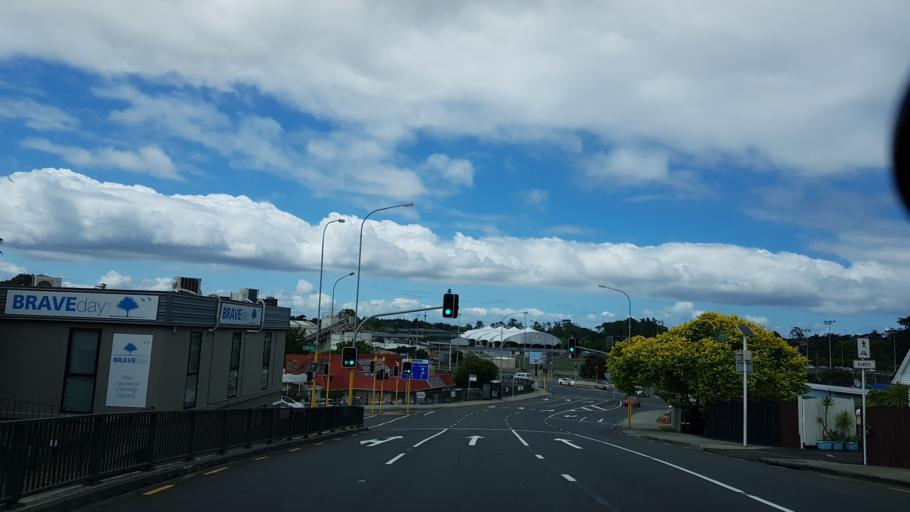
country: NZ
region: Auckland
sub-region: Auckland
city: North Shore
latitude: -36.7789
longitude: 174.7502
